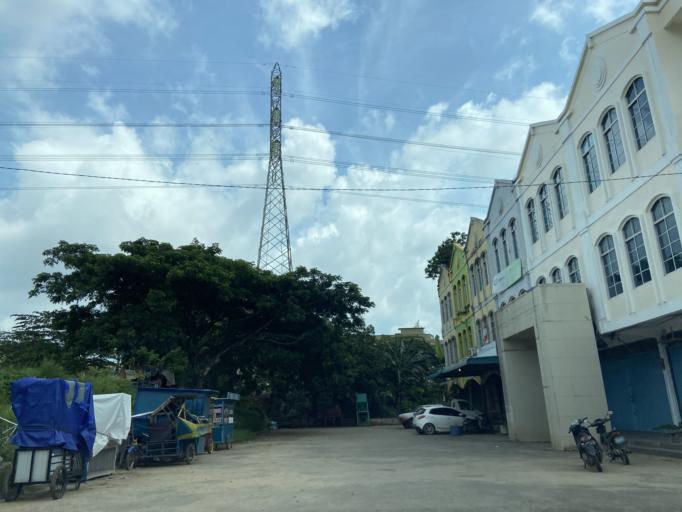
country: SG
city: Singapore
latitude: 1.1352
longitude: 104.0284
